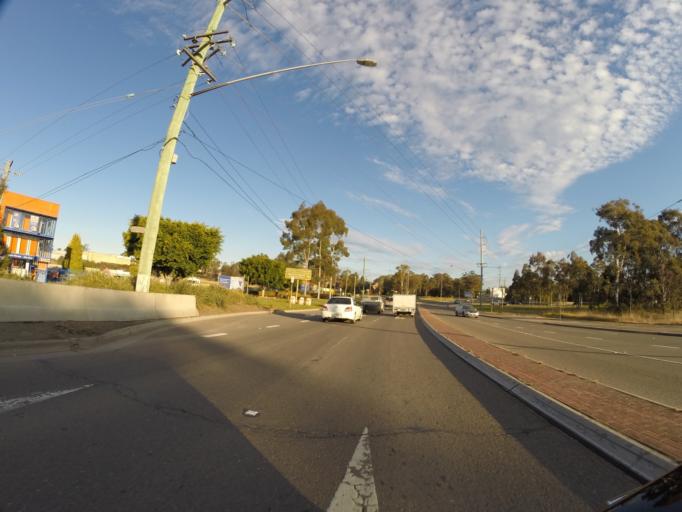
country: AU
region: New South Wales
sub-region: Fairfield
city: Horsley Park
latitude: -33.8500
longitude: 150.8768
